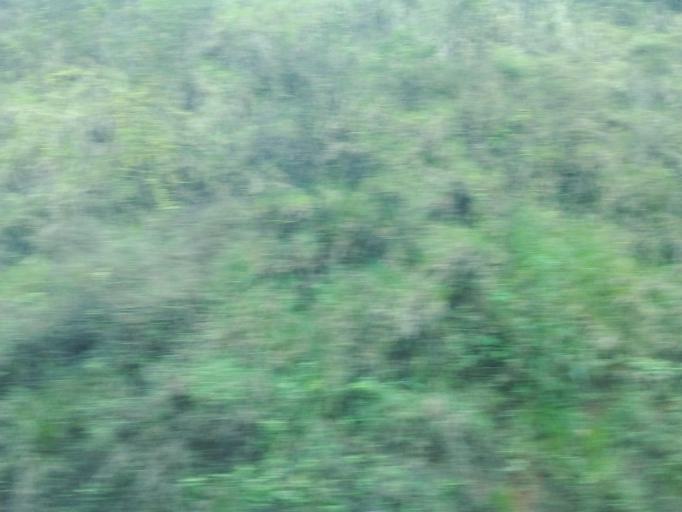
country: BR
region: Minas Gerais
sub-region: Joao Monlevade
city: Joao Monlevade
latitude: -19.8689
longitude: -43.1207
